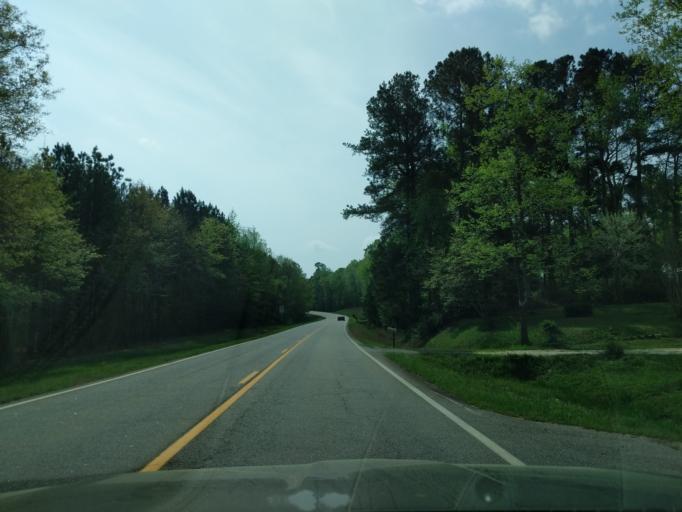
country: US
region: Georgia
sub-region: Lincoln County
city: Lincolnton
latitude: 33.7773
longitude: -82.3796
